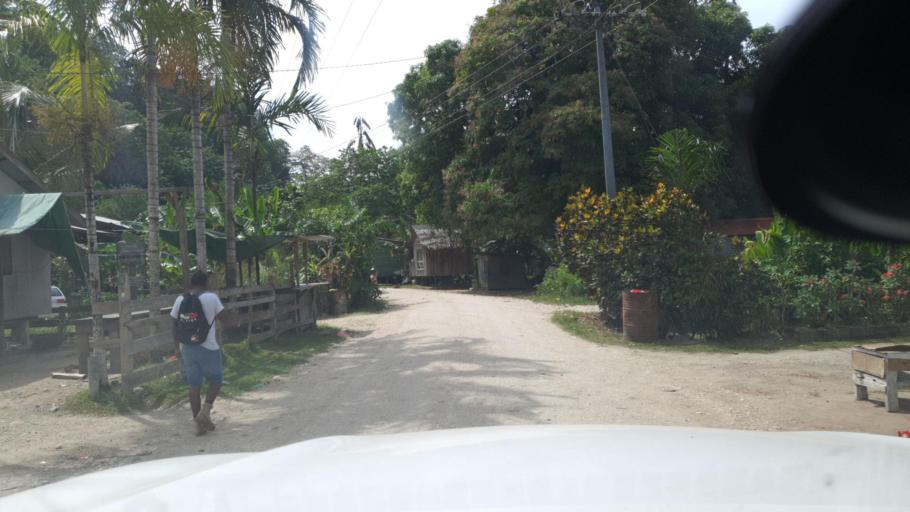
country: SB
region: Guadalcanal
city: Honiara
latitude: -9.4286
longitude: 159.9196
